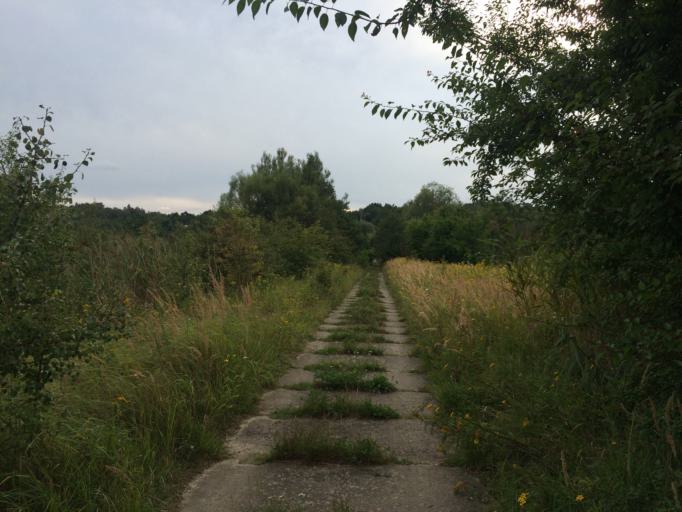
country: PL
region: Swietokrzyskie
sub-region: Powiat starachowicki
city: Starachowice
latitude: 51.0535
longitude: 21.0430
